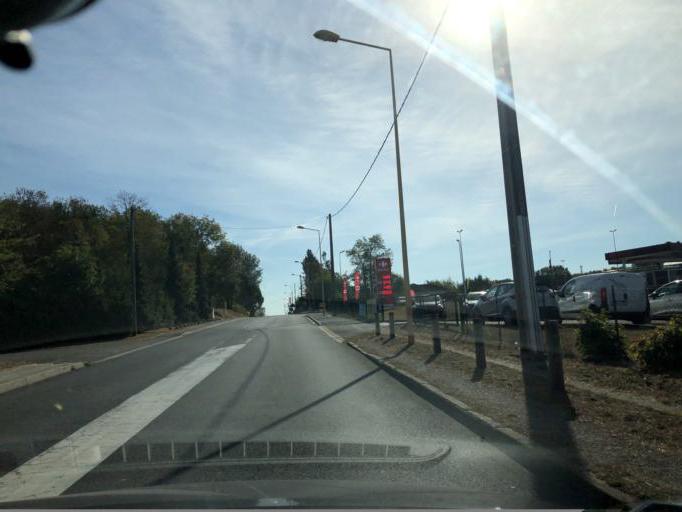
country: FR
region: Centre
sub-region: Departement du Loiret
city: Malesherbes
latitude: 48.2970
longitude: 2.3900
